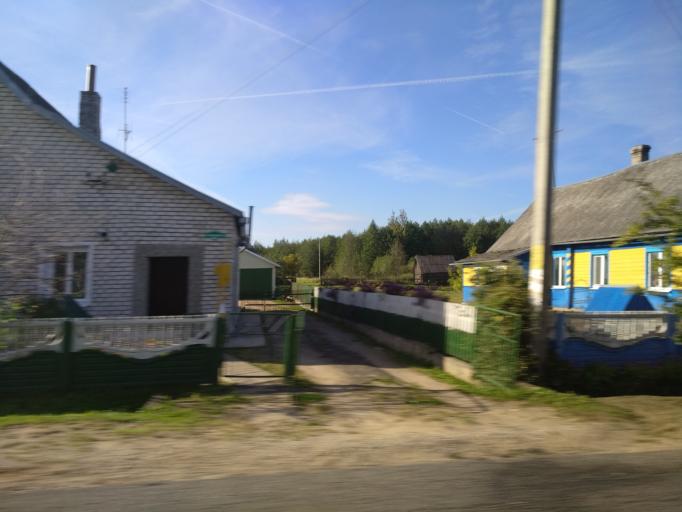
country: BY
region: Vitebsk
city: Mosar
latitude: 55.1408
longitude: 27.1905
